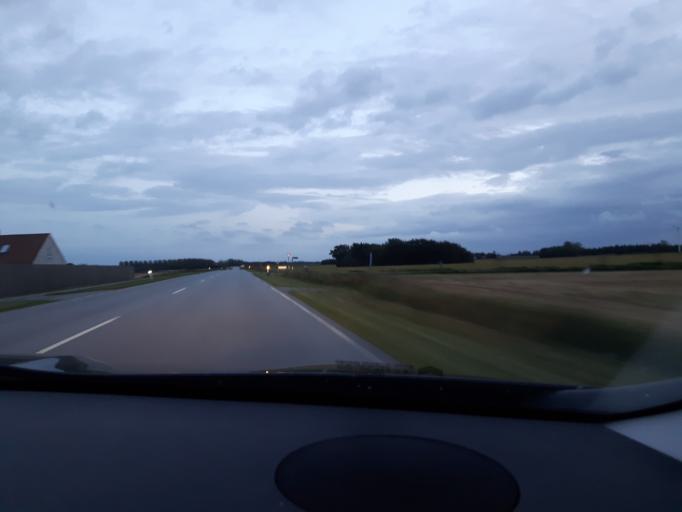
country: DK
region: North Denmark
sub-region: Hjorring Kommune
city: Hjorring
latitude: 57.4915
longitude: 9.9457
